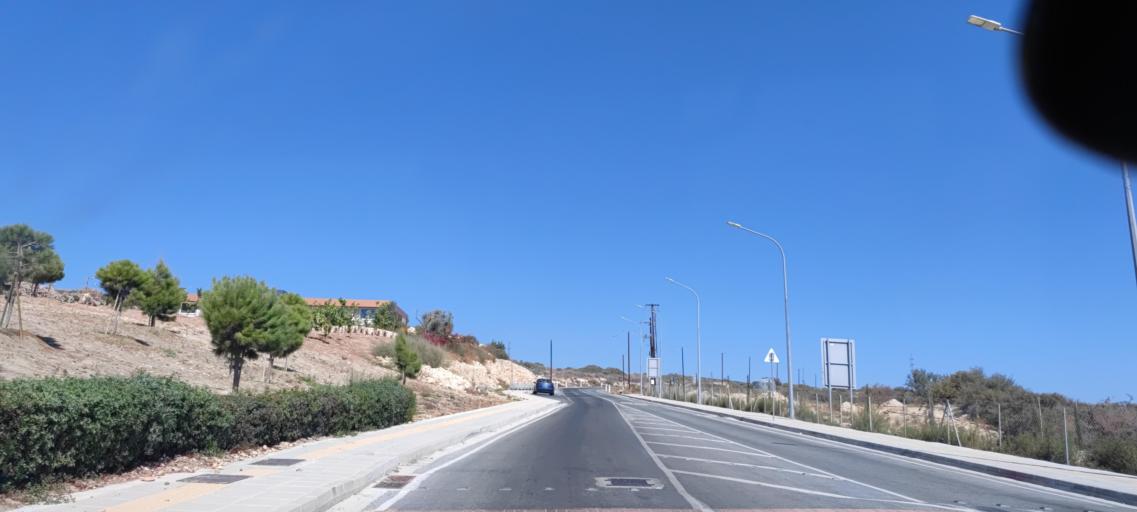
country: CY
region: Limassol
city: Mouttagiaka
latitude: 34.7297
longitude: 33.0615
